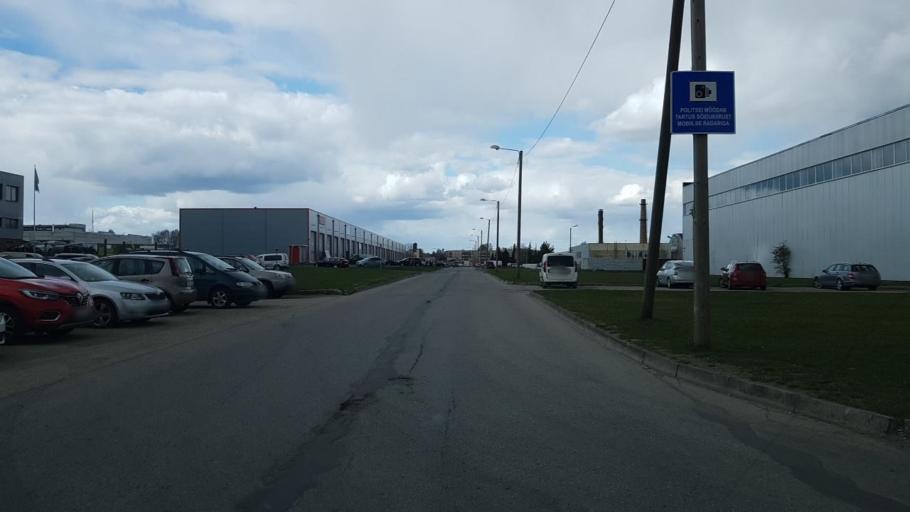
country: EE
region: Tartu
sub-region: UElenurme vald
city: Ulenurme
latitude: 58.3395
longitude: 26.7252
